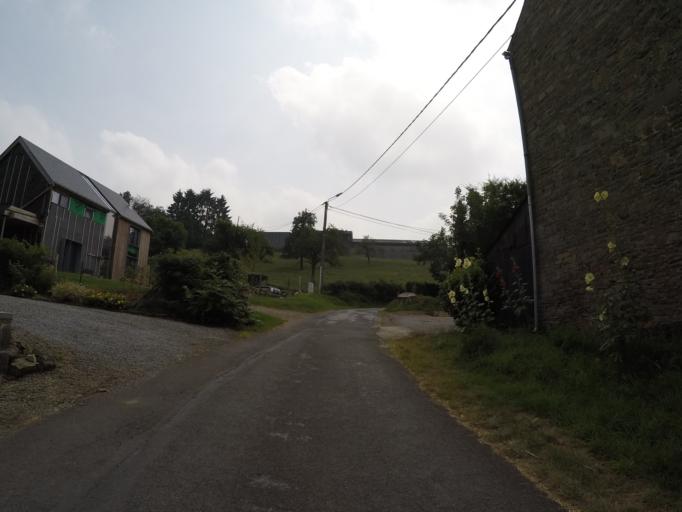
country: BE
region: Wallonia
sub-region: Province de Namur
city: Assesse
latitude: 50.3400
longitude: 4.9712
